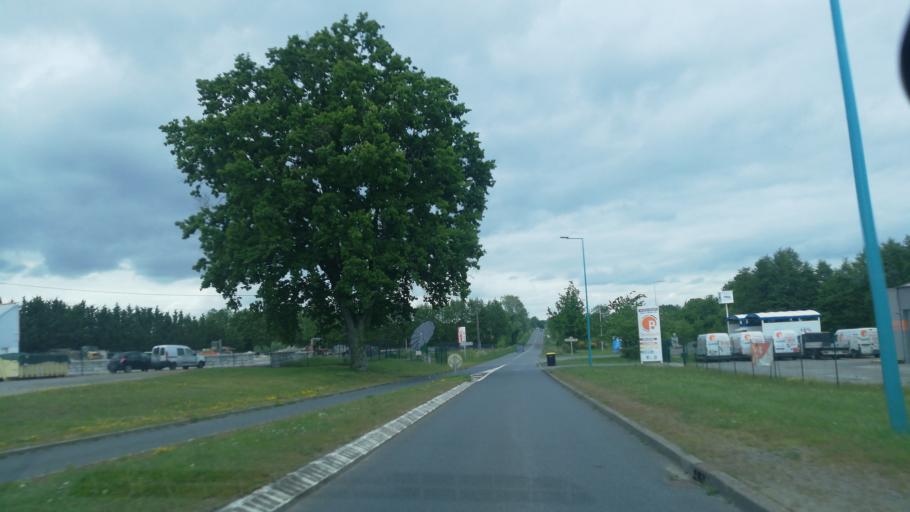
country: FR
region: Poitou-Charentes
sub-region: Departement des Deux-Sevres
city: Moncoutant
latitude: 46.7314
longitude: -0.5790
